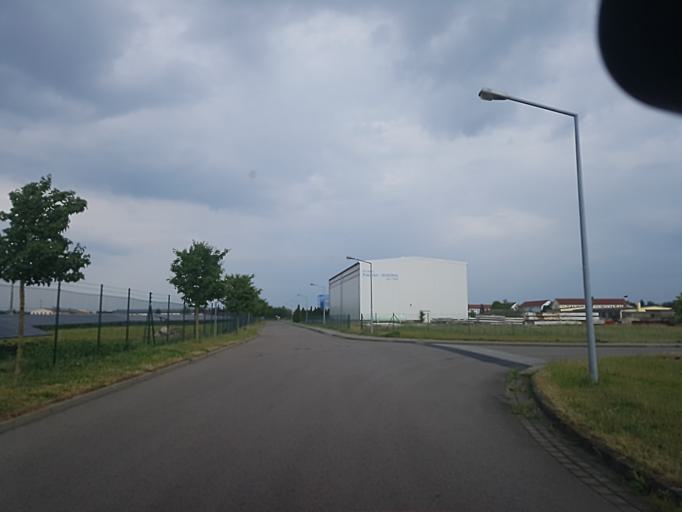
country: DE
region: Saxony-Anhalt
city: Elster
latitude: 51.8332
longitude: 12.8097
